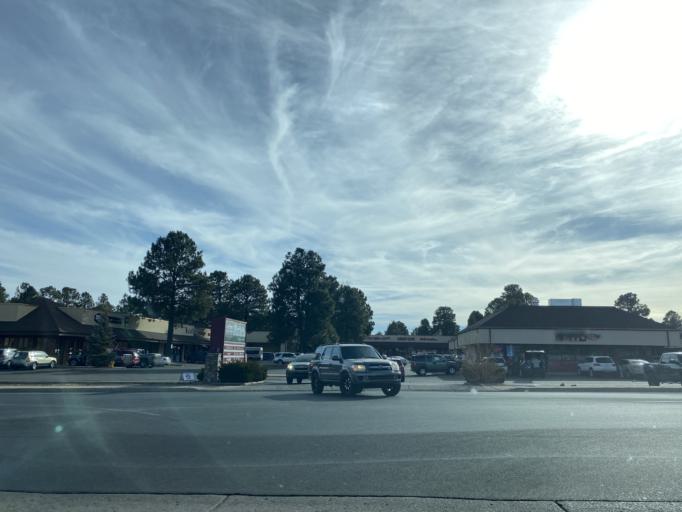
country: US
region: Arizona
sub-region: Coconino County
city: Flagstaff
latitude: 35.1835
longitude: -111.6601
